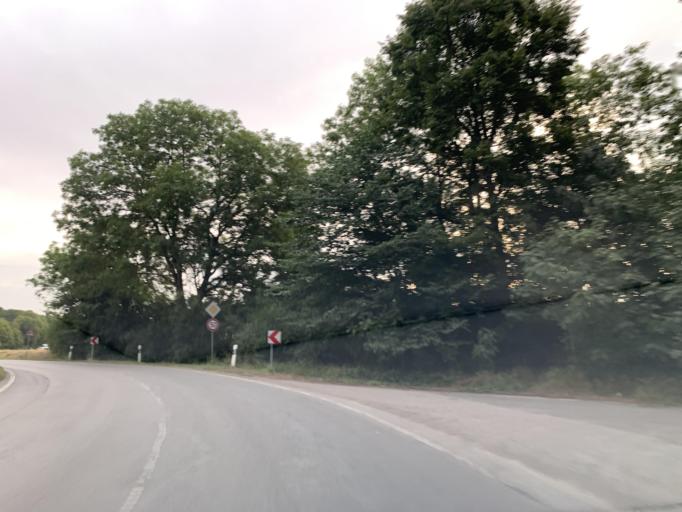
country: DE
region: Mecklenburg-Vorpommern
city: Neverin
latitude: 53.5835
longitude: 13.3272
